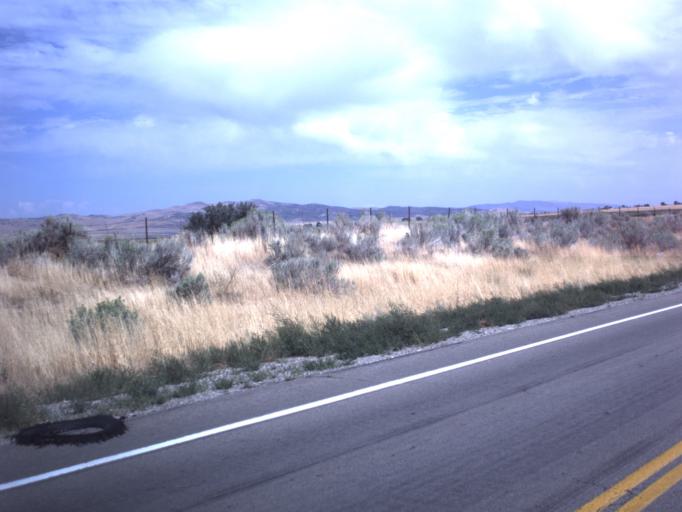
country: US
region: Utah
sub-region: Juab County
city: Nephi
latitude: 39.5237
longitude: -111.8674
